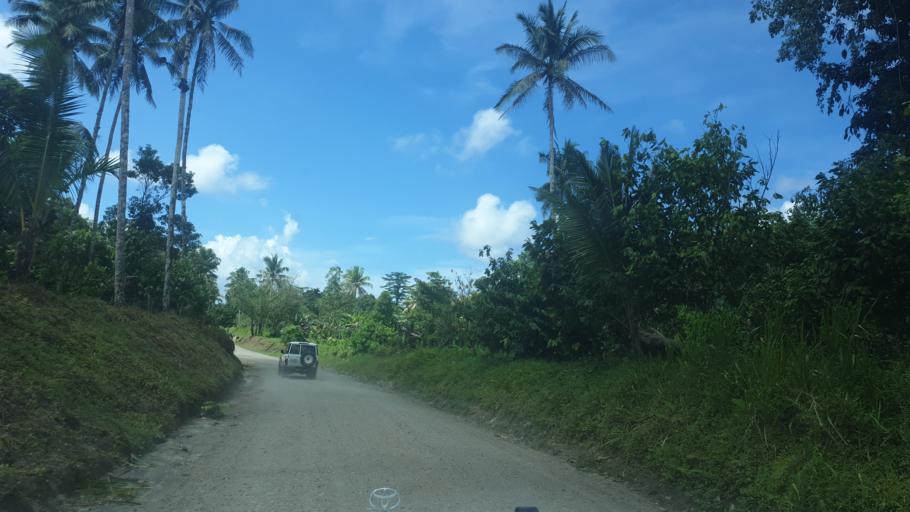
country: PG
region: Bougainville
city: Panguna
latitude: -6.7389
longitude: 155.6632
